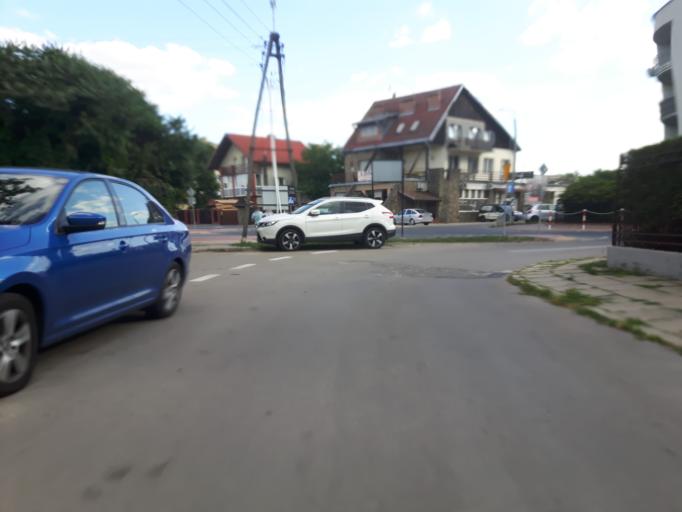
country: PL
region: Masovian Voivodeship
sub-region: Powiat wolominski
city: Zabki
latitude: 52.2927
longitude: 21.1179
